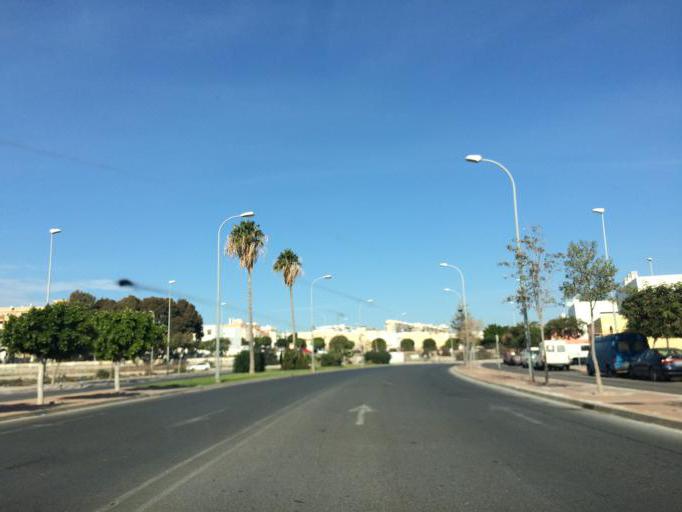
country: ES
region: Andalusia
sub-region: Provincia de Almeria
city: Almeria
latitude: 36.8467
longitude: -2.4341
